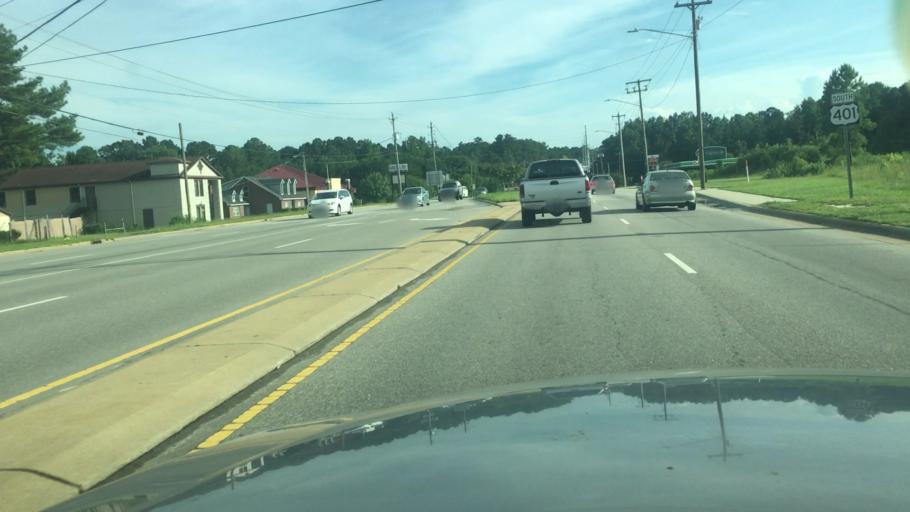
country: US
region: North Carolina
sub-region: Cumberland County
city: Eastover
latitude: 35.1538
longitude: -78.8701
